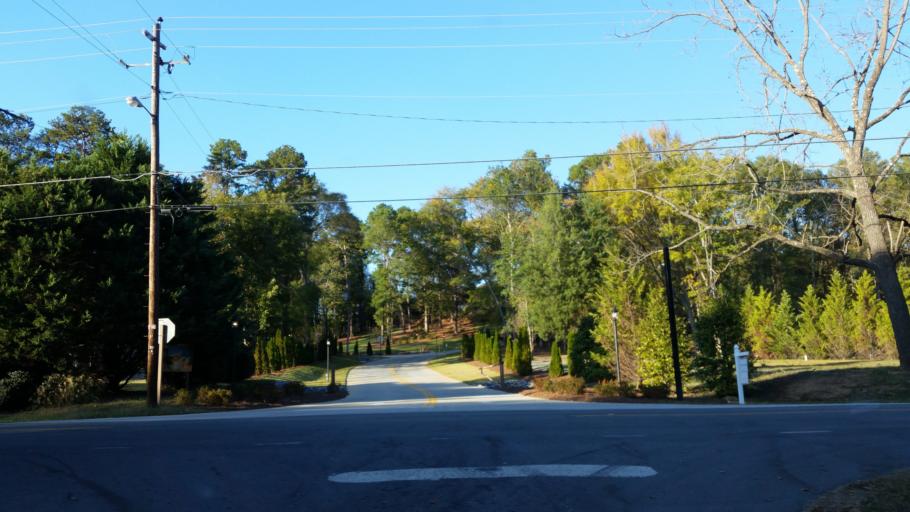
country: US
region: Georgia
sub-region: Bartow County
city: Euharlee
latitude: 34.2381
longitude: -84.9436
